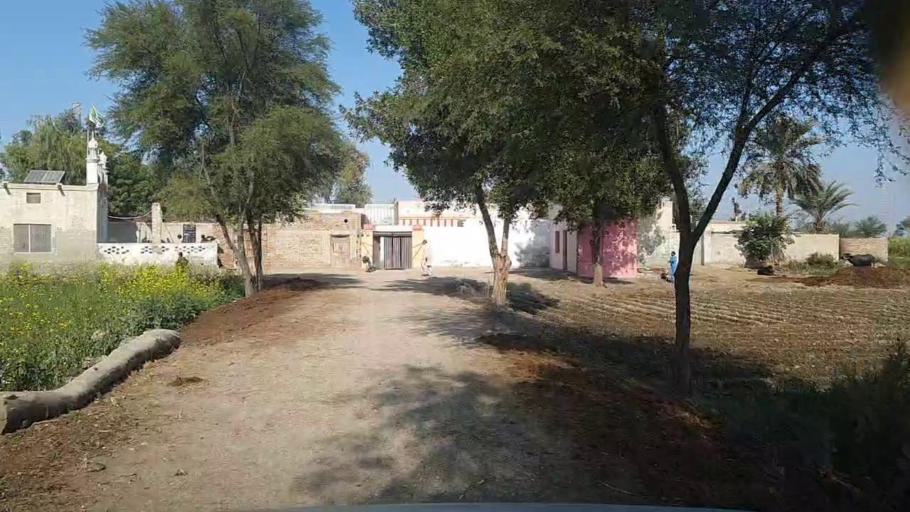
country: PK
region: Sindh
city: Khairpur
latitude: 28.0594
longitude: 69.6741
